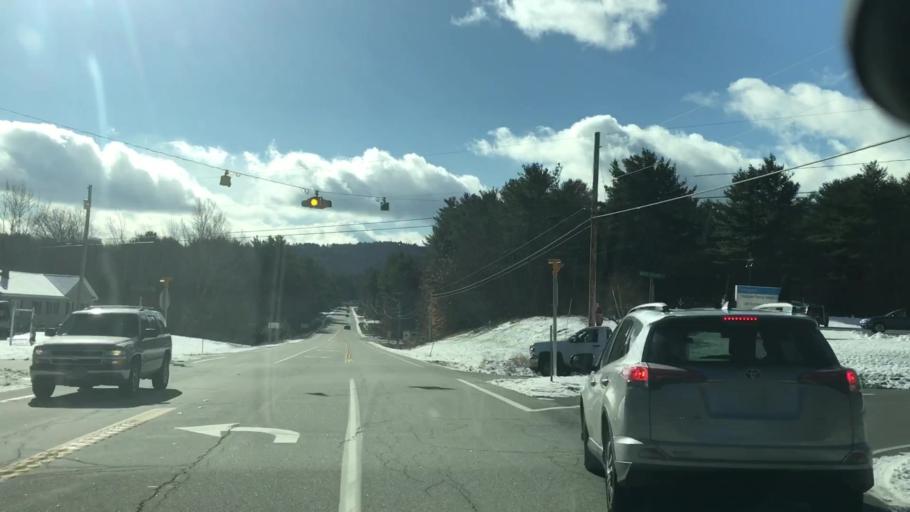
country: US
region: New Hampshire
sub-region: Carroll County
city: Ossipee
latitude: 43.6869
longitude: -71.1211
